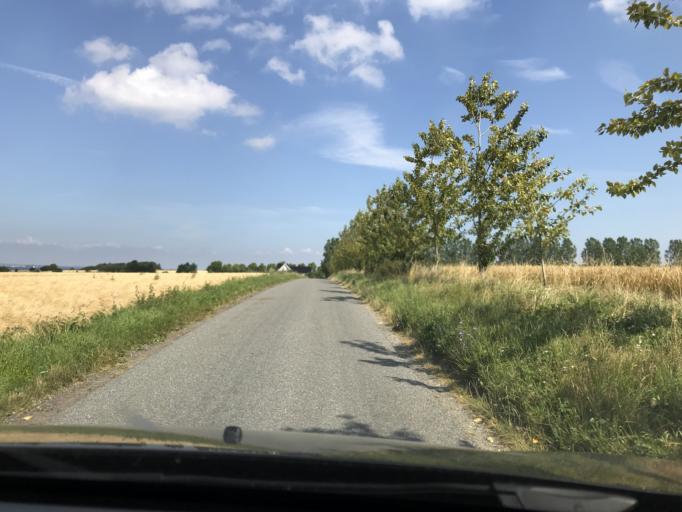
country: DK
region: South Denmark
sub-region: AEro Kommune
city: AEroskobing
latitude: 54.8863
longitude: 10.3934
